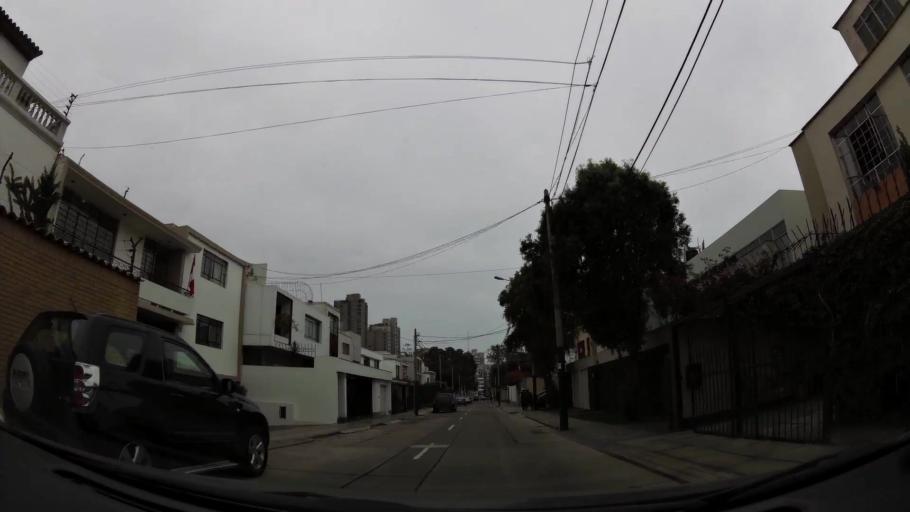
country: PE
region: Lima
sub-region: Lima
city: San Isidro
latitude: -12.0966
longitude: -77.0526
